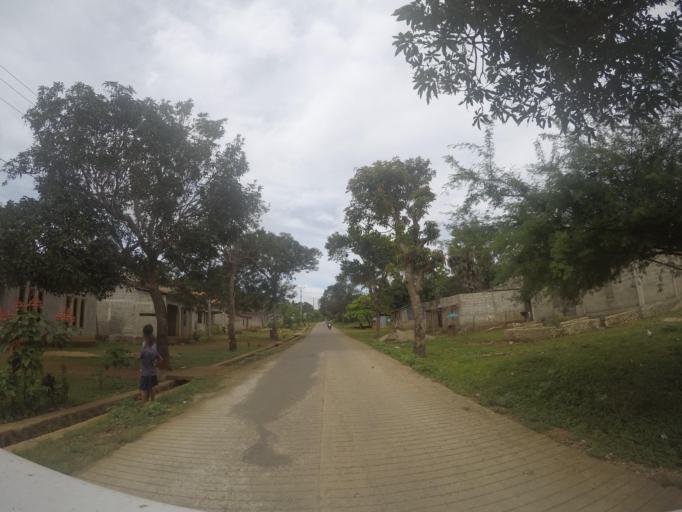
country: TL
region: Lautem
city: Lospalos
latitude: -8.5086
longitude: 126.9809
